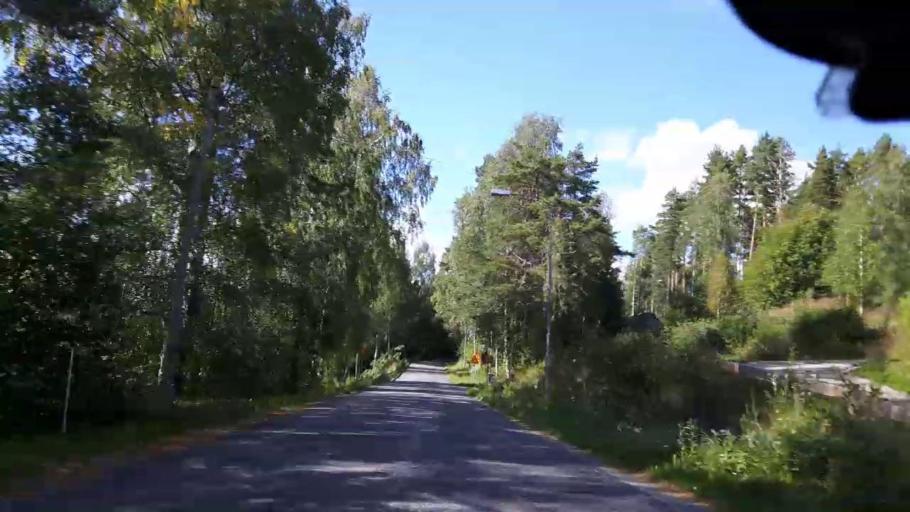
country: SE
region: Jaemtland
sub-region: Braecke Kommun
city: Braecke
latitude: 63.1782
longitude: 15.5577
